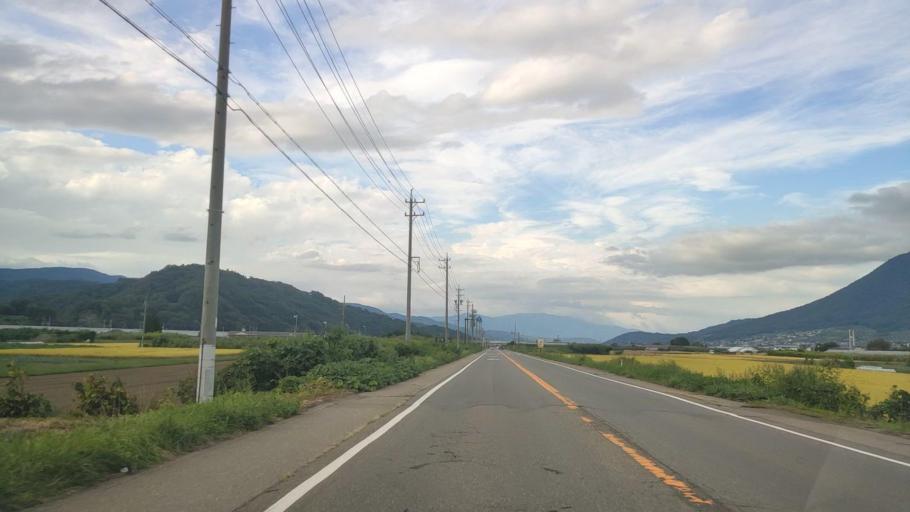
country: JP
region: Nagano
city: Nakano
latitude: 36.7734
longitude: 138.3505
